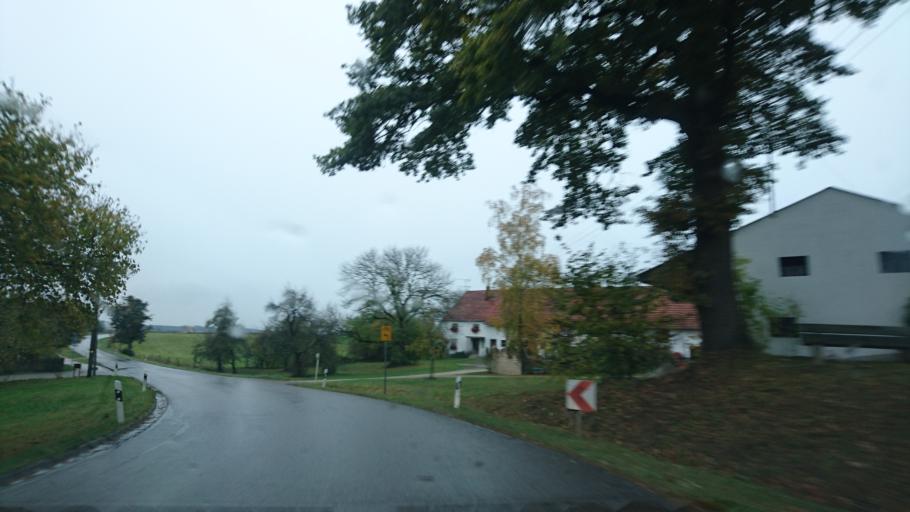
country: DE
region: Bavaria
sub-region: Upper Bavaria
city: Hilgertshausen-Tandern
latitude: 48.4334
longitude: 11.3246
